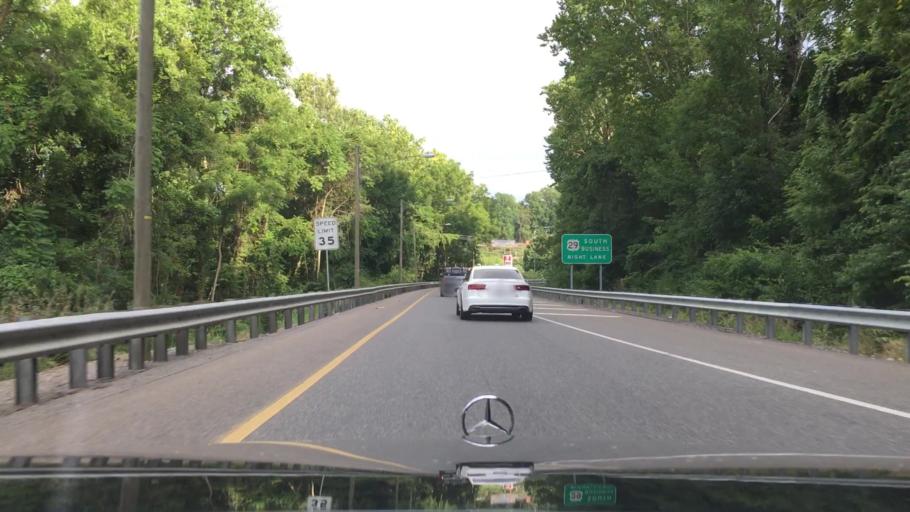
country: US
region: Virginia
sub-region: City of Lynchburg
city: West Lynchburg
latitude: 37.3612
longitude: -79.1828
